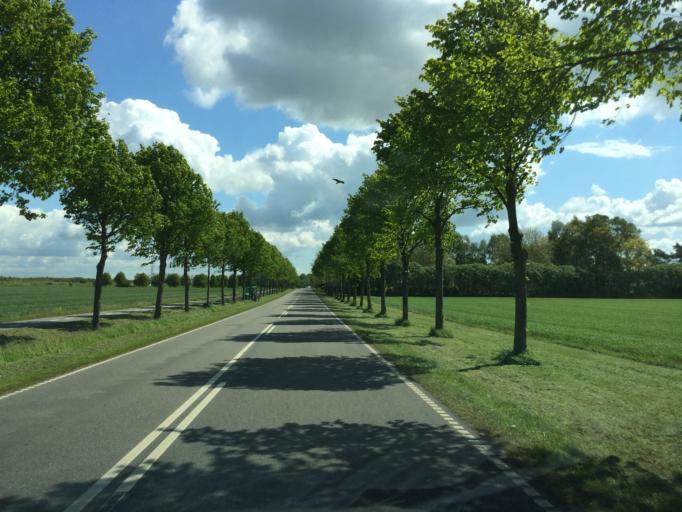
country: DK
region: Zealand
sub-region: Roskilde Kommune
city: Svogerslev
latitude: 55.6229
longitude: 12.0408
